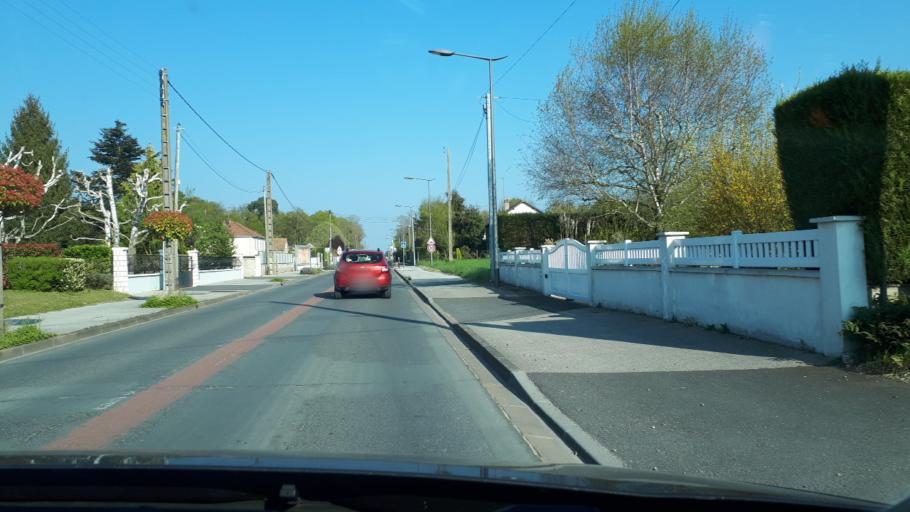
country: FR
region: Centre
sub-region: Departement d'Indre-et-Loire
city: Blere
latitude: 47.3246
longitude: 1.0083
